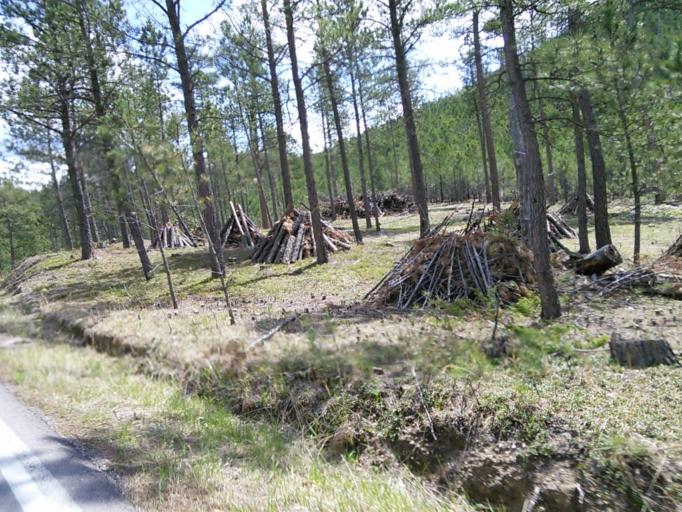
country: US
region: South Dakota
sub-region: Custer County
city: Custer
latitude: 43.7900
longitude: -103.4462
